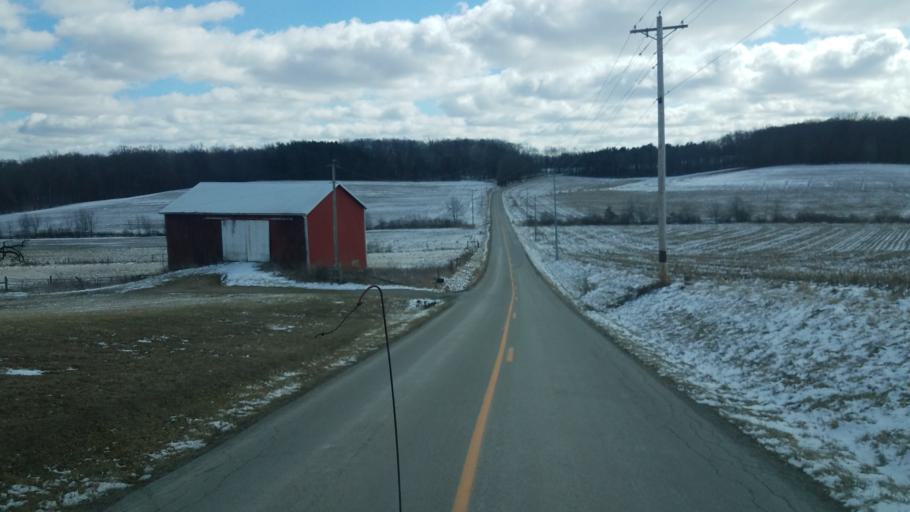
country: US
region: Ohio
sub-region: Sandusky County
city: Bellville
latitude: 40.5927
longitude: -82.3712
